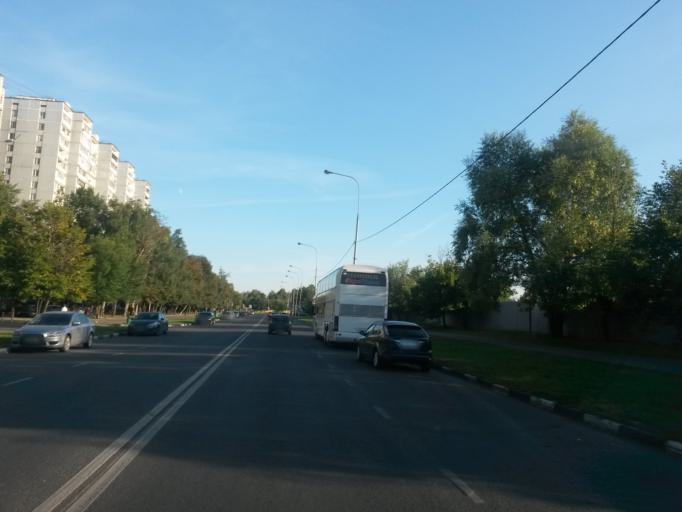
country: RU
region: Moscow
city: Orekhovo-Borisovo
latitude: 55.6054
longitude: 37.7251
